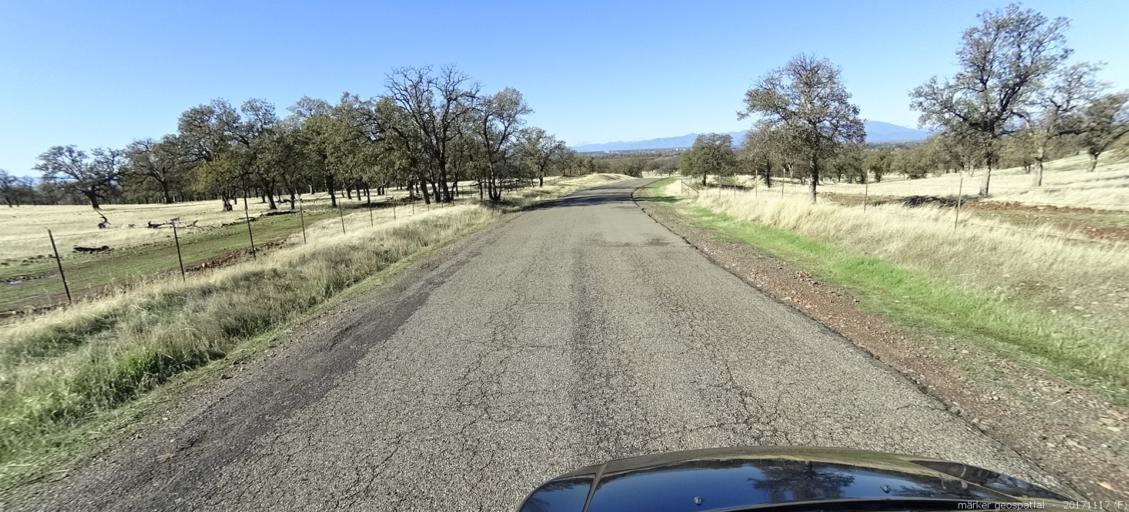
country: US
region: California
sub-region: Shasta County
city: Cottonwood
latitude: 40.4251
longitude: -122.1777
